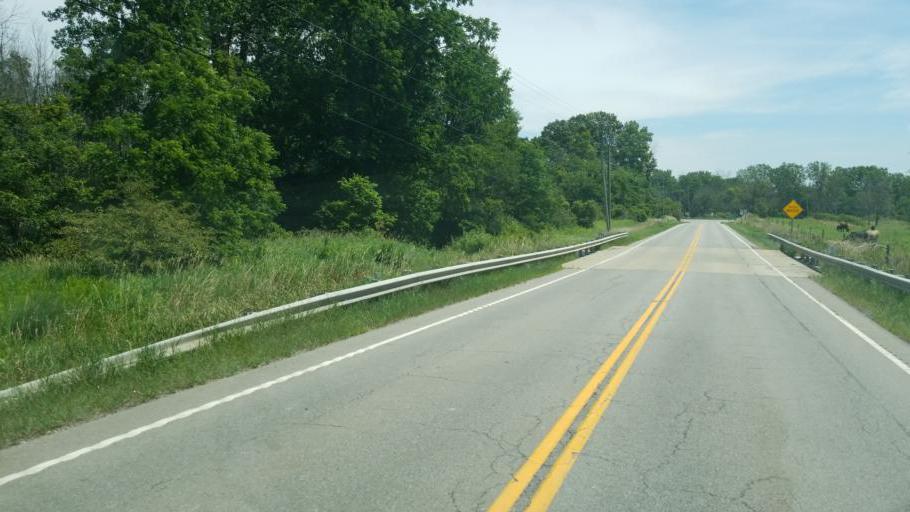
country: US
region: Ohio
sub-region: Richland County
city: Lincoln Heights
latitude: 40.8867
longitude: -82.5155
